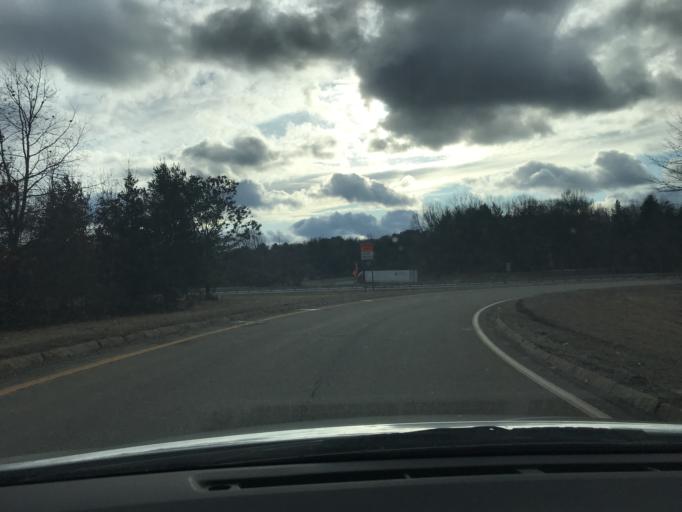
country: US
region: Massachusetts
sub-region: Middlesex County
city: Littleton Common
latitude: 42.5207
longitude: -71.5057
